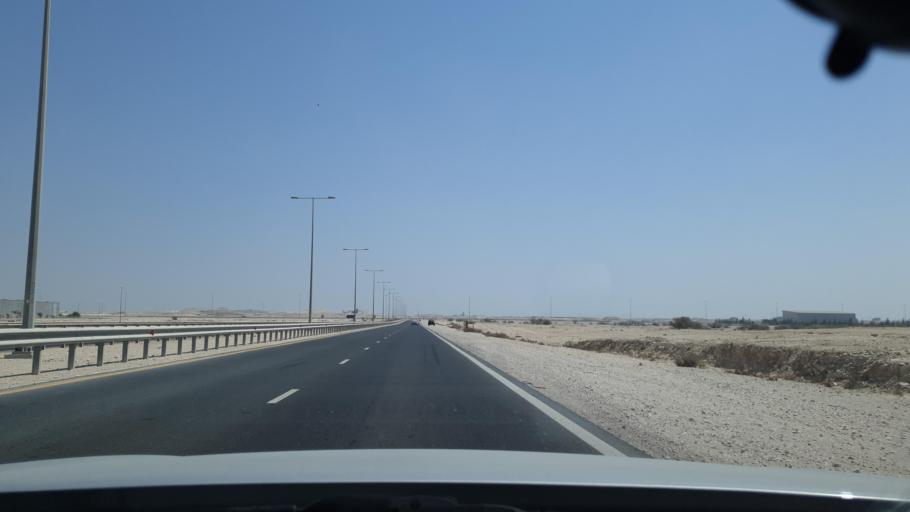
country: QA
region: Baladiyat Umm Salal
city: Umm Salal Muhammad
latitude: 25.3871
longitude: 51.3533
